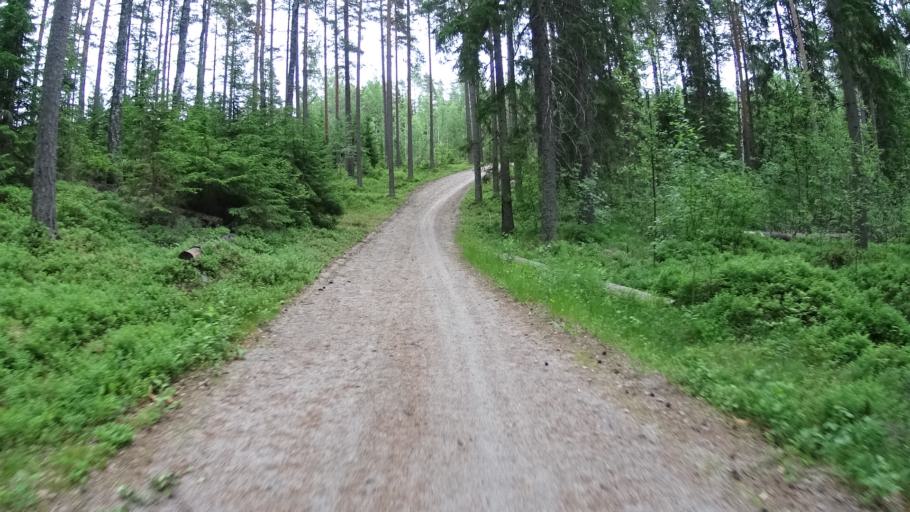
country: FI
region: Uusimaa
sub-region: Helsinki
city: Espoo
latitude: 60.2905
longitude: 24.5905
